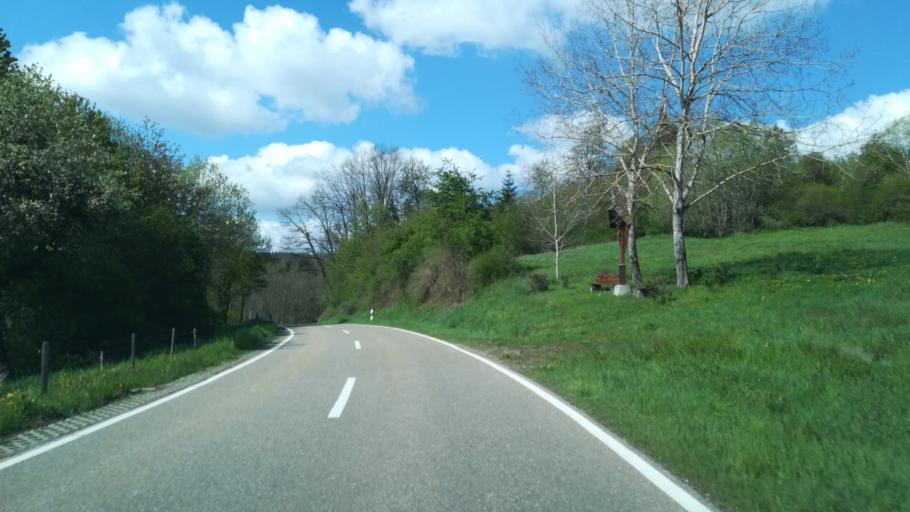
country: DE
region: Baden-Wuerttemberg
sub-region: Freiburg Region
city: Uhlingen-Birkendorf
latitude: 47.7518
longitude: 8.3524
